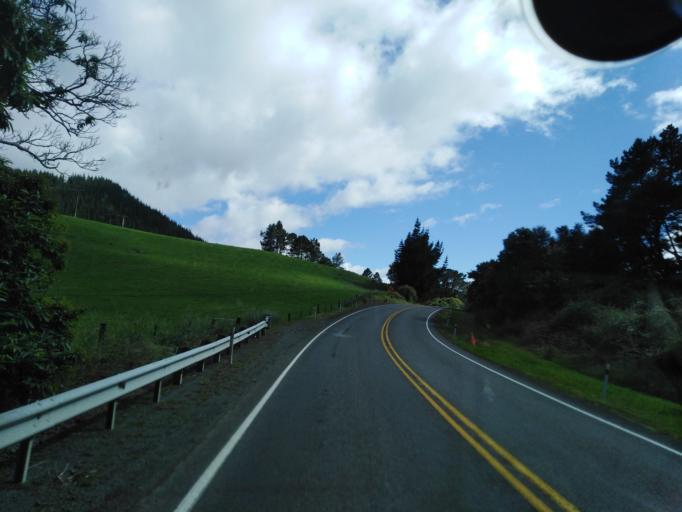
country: NZ
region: Nelson
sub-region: Nelson City
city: Nelson
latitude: -41.2881
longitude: 173.5715
